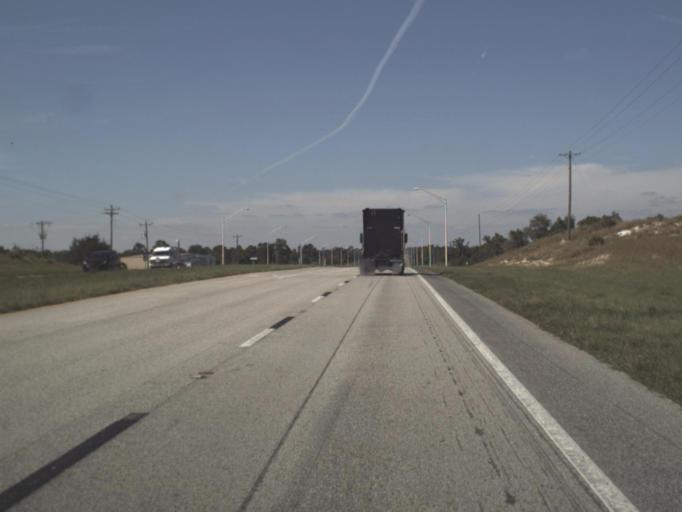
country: US
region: Florida
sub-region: Highlands County
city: Lake Placid
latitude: 27.3684
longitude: -81.3980
